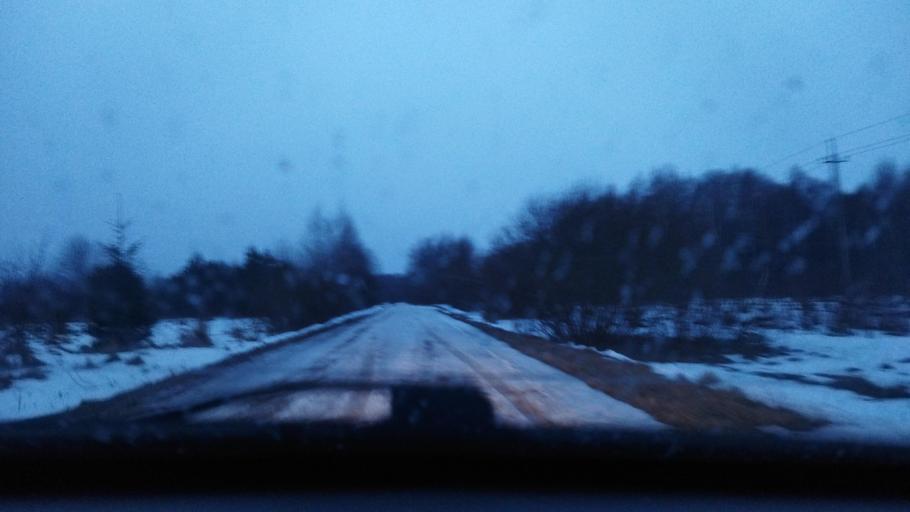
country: BY
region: Minsk
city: Svir
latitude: 54.9383
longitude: 26.3981
